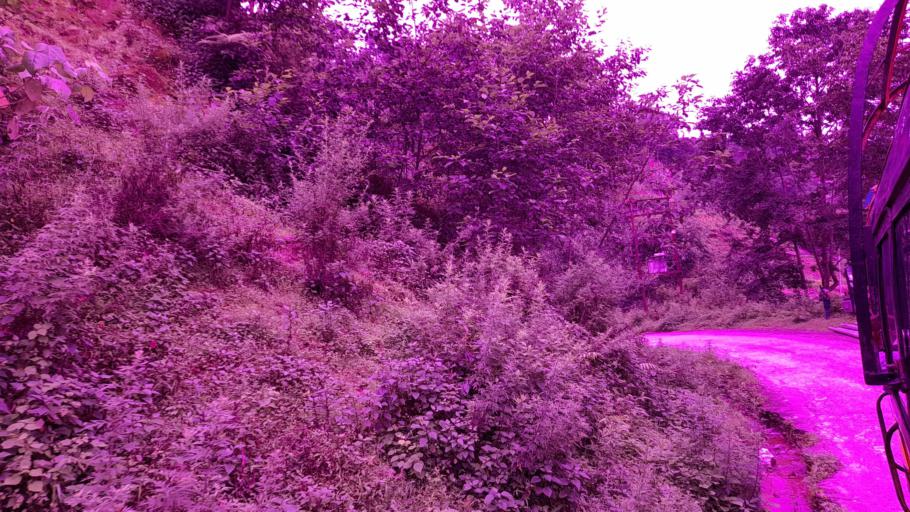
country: NP
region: Central Region
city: Kirtipur
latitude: 27.8253
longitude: 85.2095
